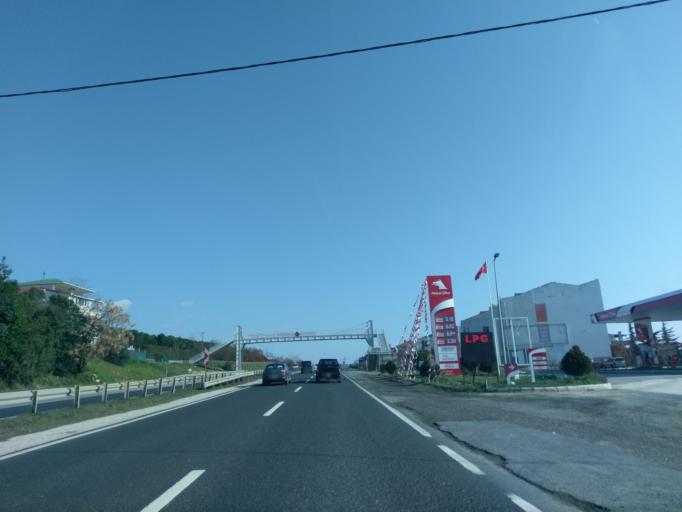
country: TR
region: Istanbul
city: Kumburgaz
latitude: 41.0184
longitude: 28.4830
